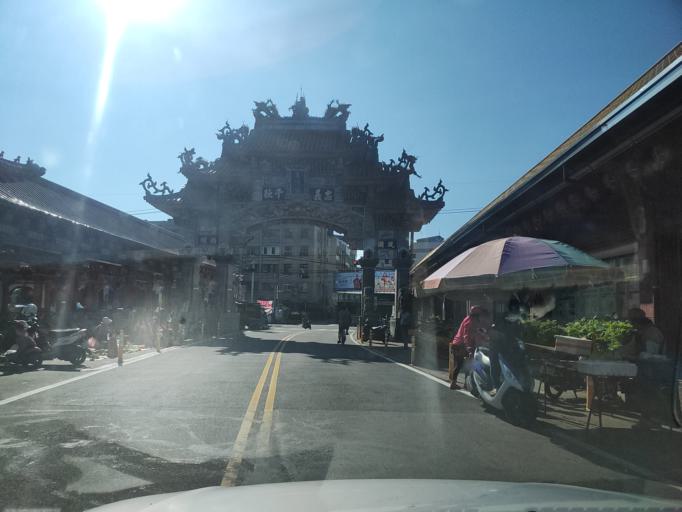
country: TW
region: Taiwan
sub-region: Miaoli
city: Miaoli
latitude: 24.5640
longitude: 120.8269
